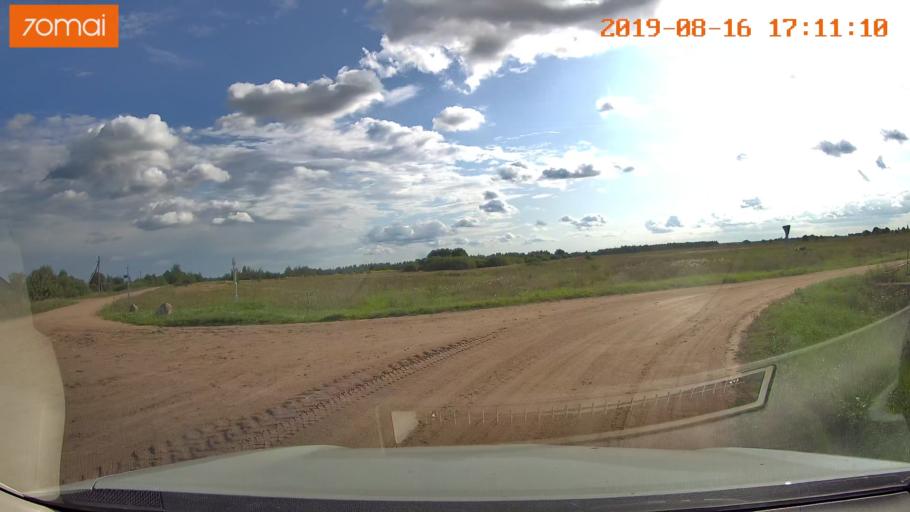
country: BY
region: Mogilev
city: Hlusha
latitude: 53.1953
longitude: 28.9092
